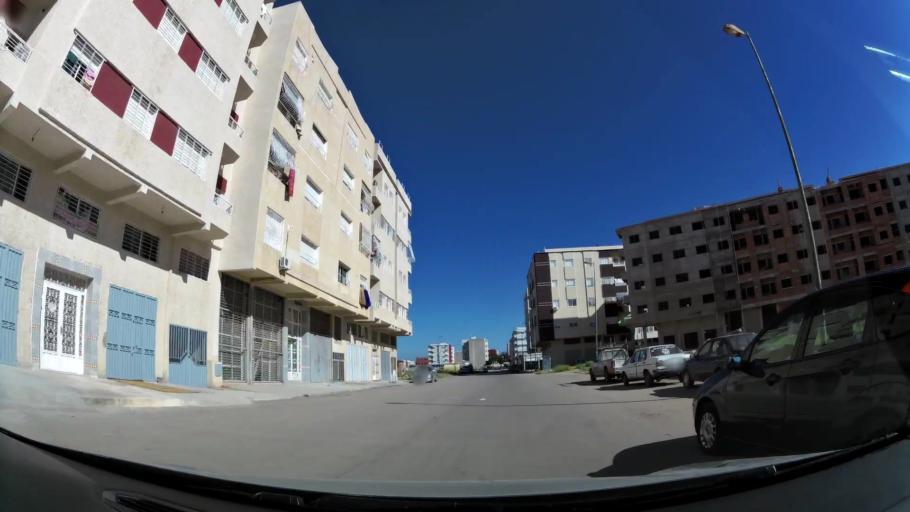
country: MA
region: Fes-Boulemane
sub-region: Fes
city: Fes
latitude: 34.0148
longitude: -4.9625
